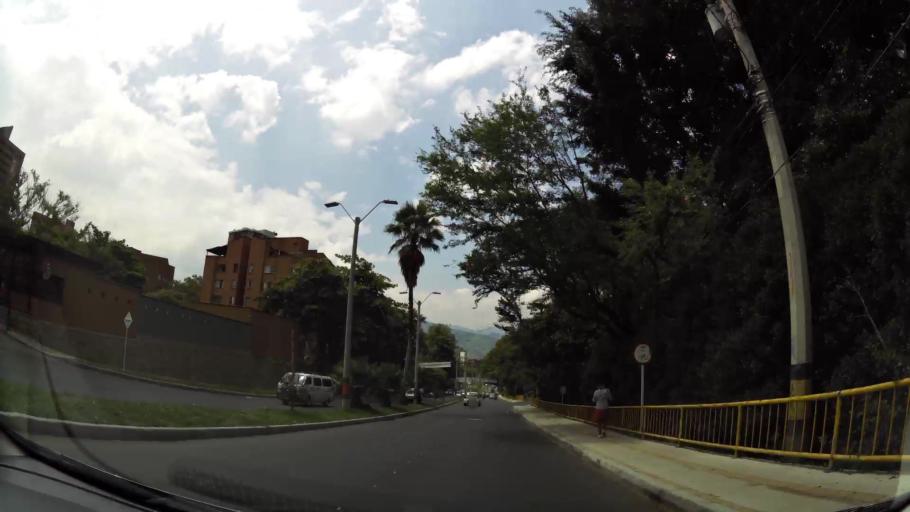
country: CO
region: Antioquia
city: Envigado
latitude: 6.1822
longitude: -75.5771
